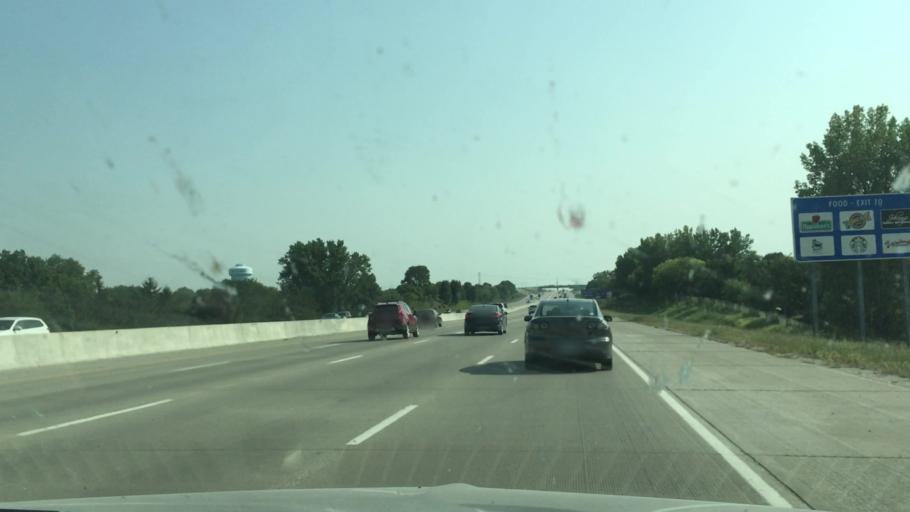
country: US
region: Iowa
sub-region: Polk County
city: Clive
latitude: 41.5725
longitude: -93.7774
